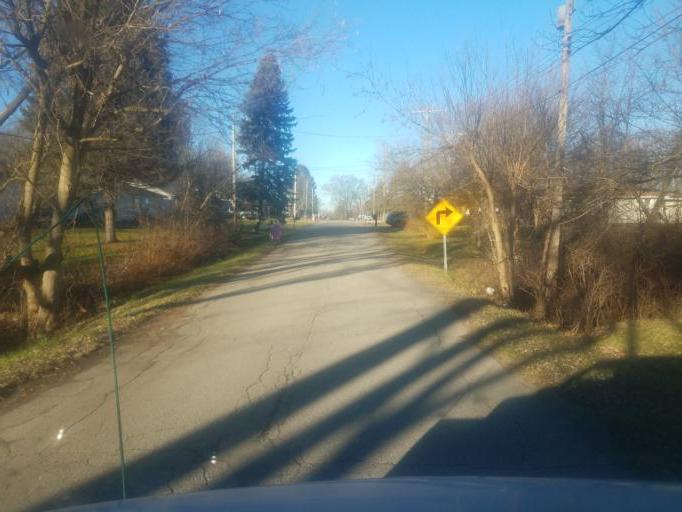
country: US
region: Ohio
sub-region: Richland County
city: Ontario
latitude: 40.7883
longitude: -82.5545
